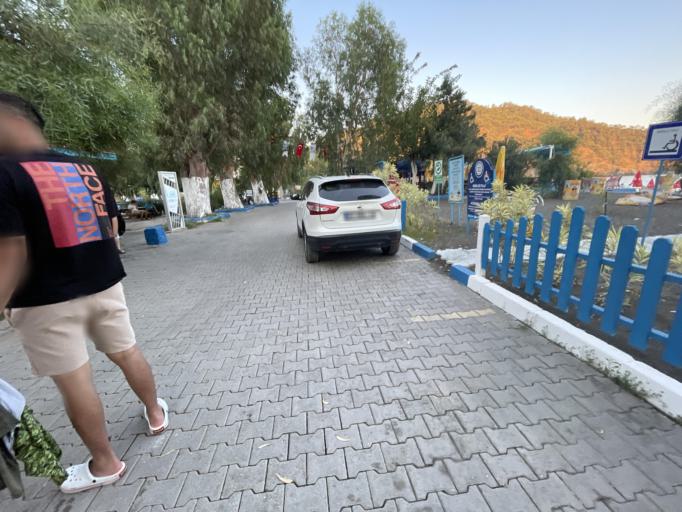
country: TR
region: Mugla
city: Goecek
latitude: 36.7312
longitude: 28.9674
